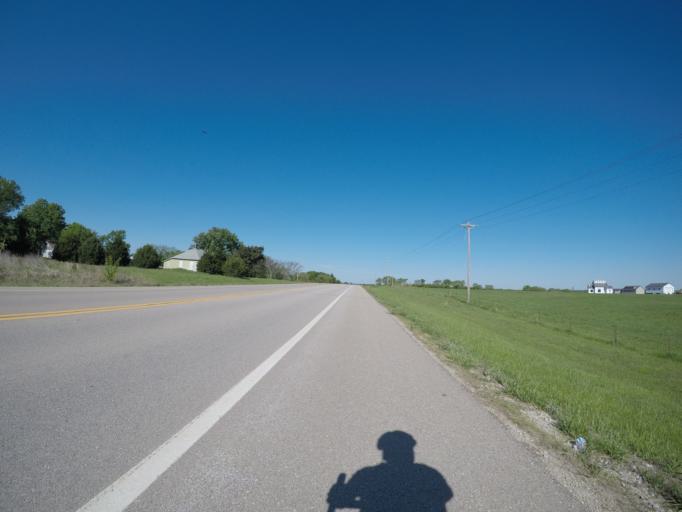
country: US
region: Kansas
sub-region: Douglas County
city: Lawrence
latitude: 38.9714
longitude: -95.4034
